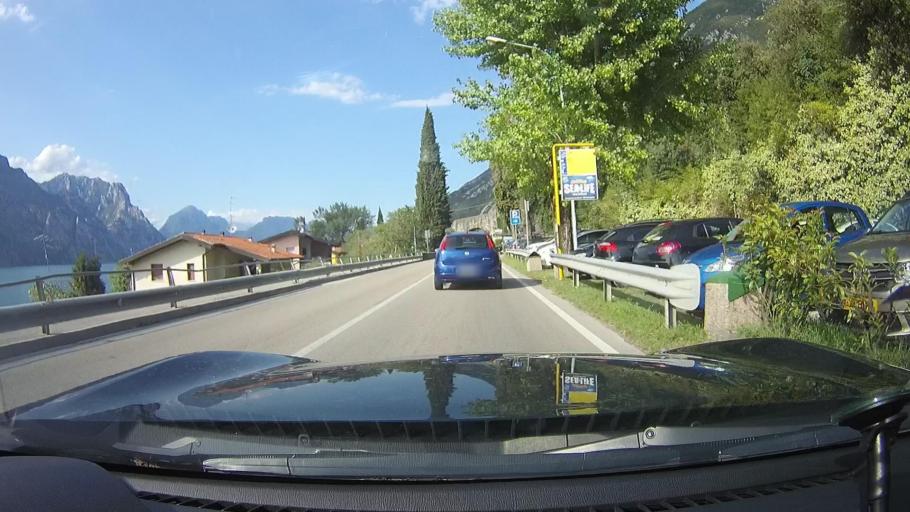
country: IT
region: Lombardy
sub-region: Provincia di Brescia
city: Limone sul Garda
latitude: 45.8071
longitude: 10.8475
